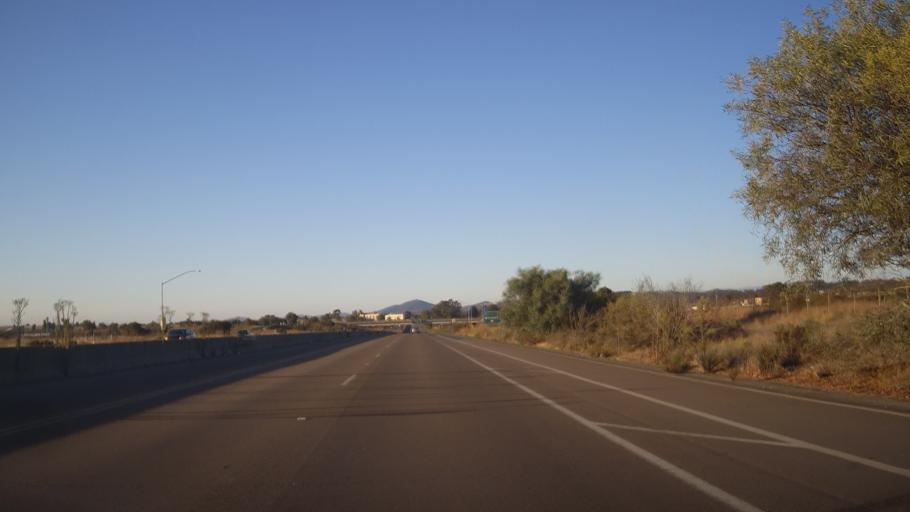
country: US
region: California
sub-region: San Diego County
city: Poway
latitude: 32.8758
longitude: -117.1165
